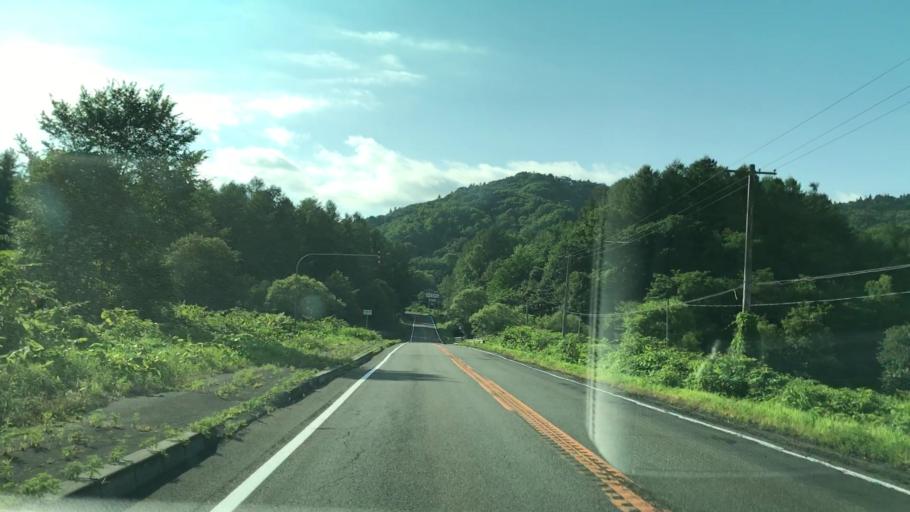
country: JP
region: Hokkaido
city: Chitose
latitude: 42.8706
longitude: 142.1532
